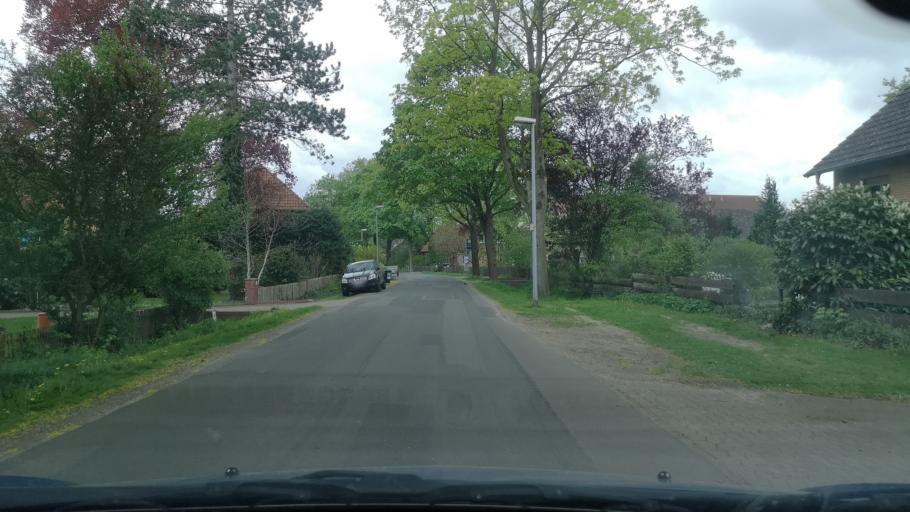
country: DE
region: Lower Saxony
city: Langenhagen
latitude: 52.4847
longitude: 9.7648
